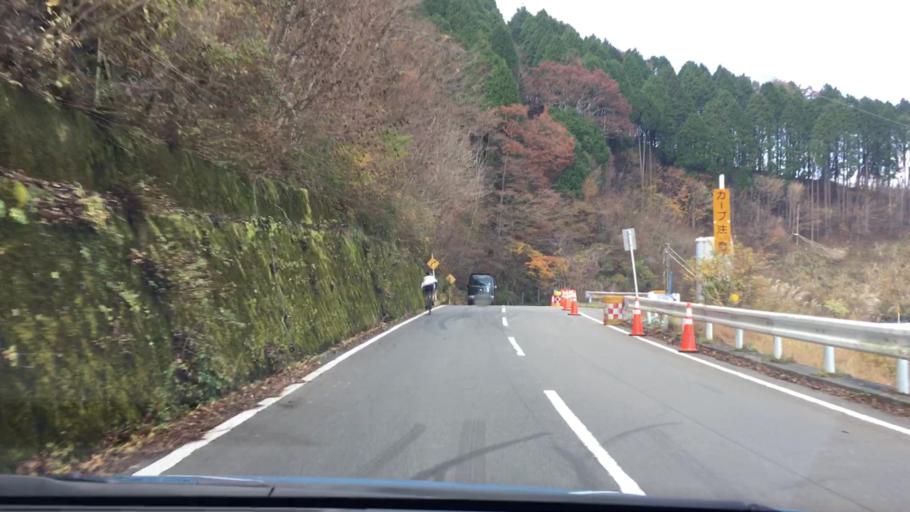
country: JP
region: Shizuoka
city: Gotemba
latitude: 35.4012
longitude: 138.9268
